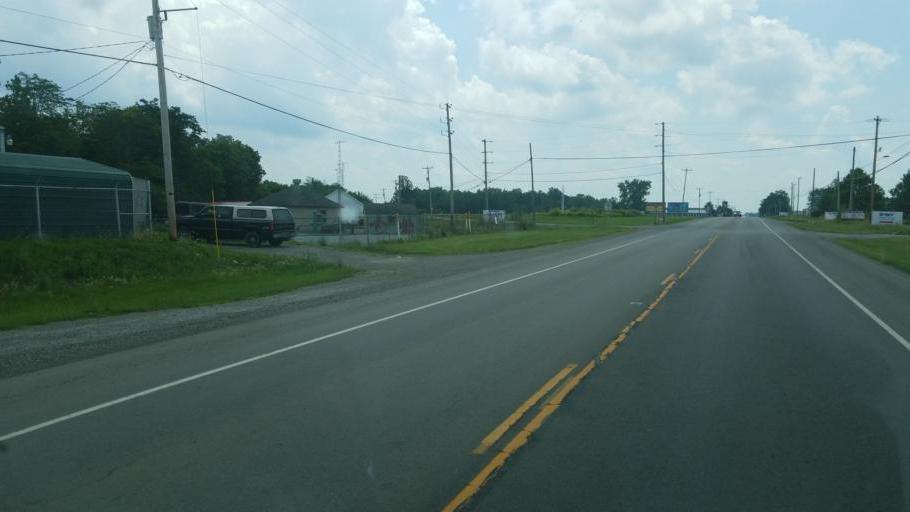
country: US
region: Ohio
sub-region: Hardin County
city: Kenton
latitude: 40.6292
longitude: -83.6173
